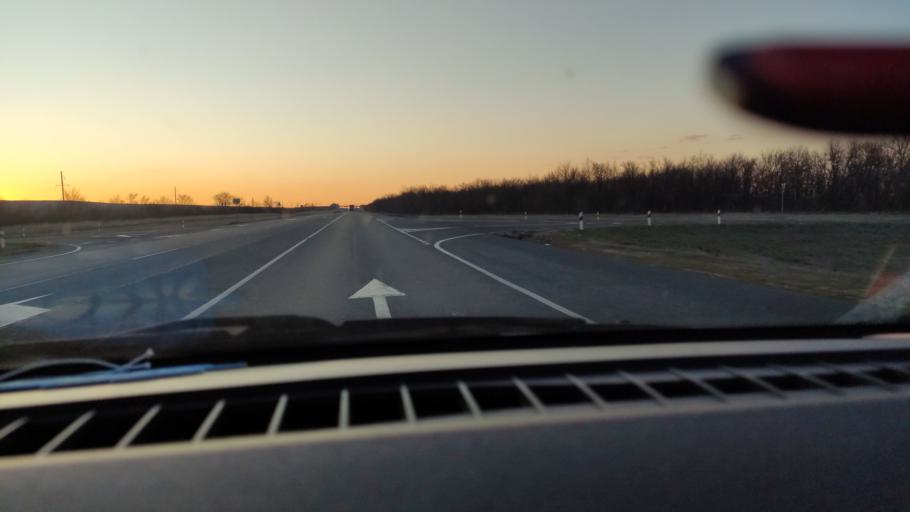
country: RU
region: Saratov
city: Yelshanka
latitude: 51.8275
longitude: 46.2677
